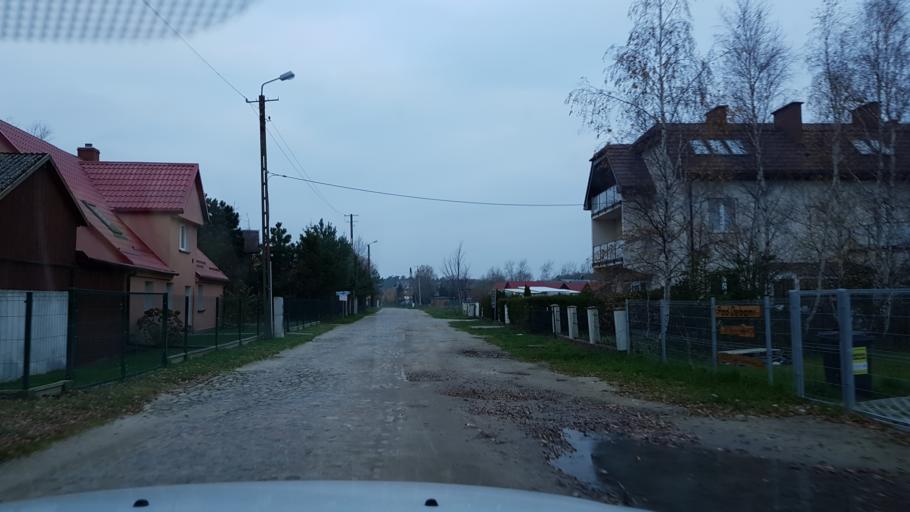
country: PL
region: West Pomeranian Voivodeship
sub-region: Powiat slawienski
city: Darlowo
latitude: 54.5071
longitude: 16.4759
